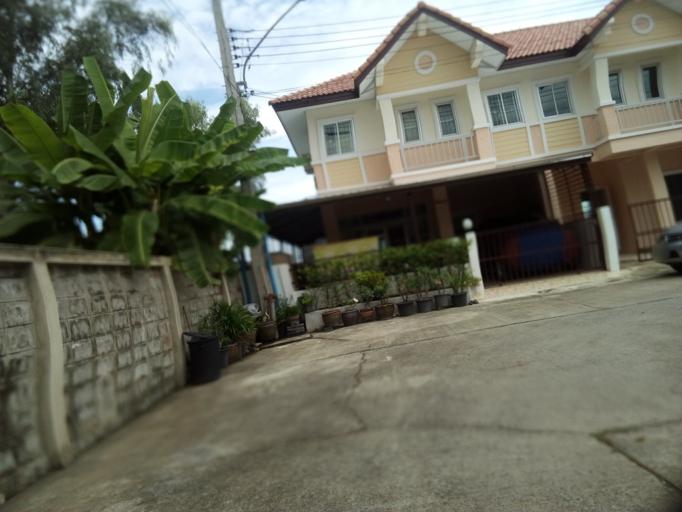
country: TH
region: Pathum Thani
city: Ban Rangsit
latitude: 14.0439
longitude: 100.8343
